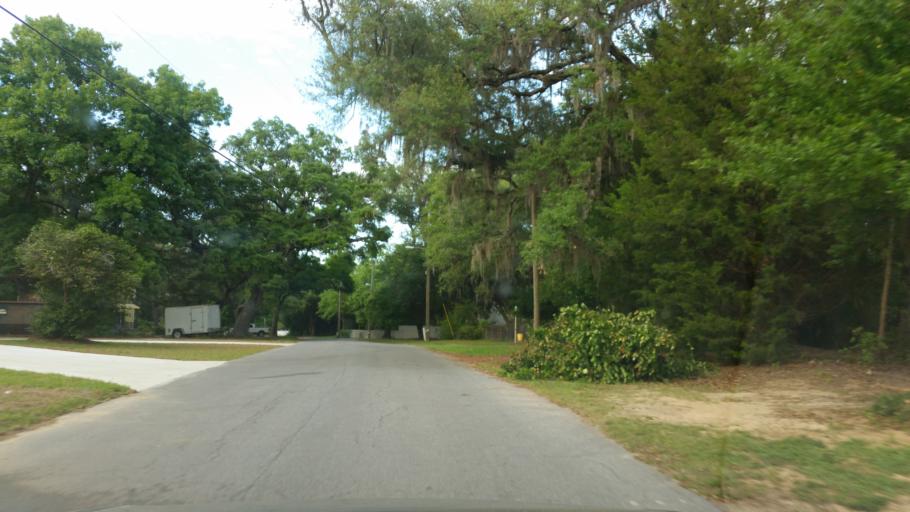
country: US
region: Florida
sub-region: Escambia County
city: East Pensacola Heights
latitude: 30.4226
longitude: -87.1822
